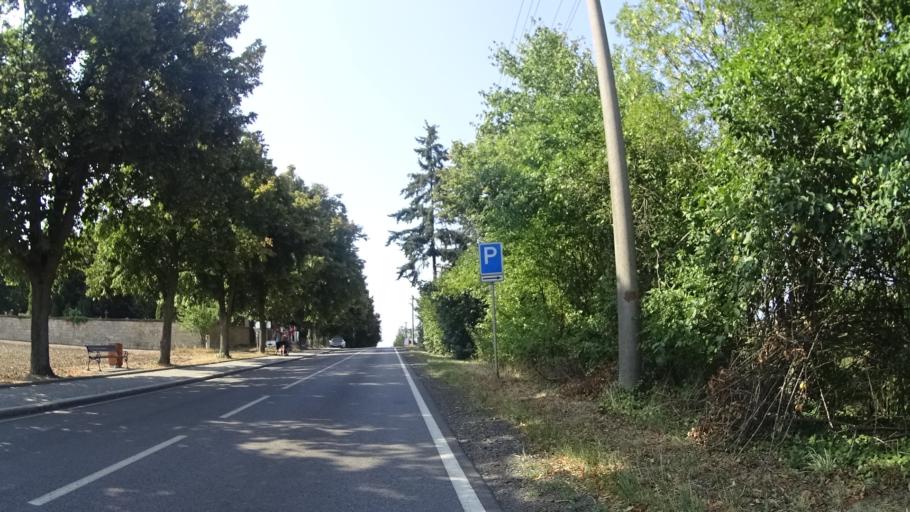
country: CZ
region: Kralovehradecky
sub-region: Okres Jicin
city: Sobotka
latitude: 50.4712
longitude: 15.1741
